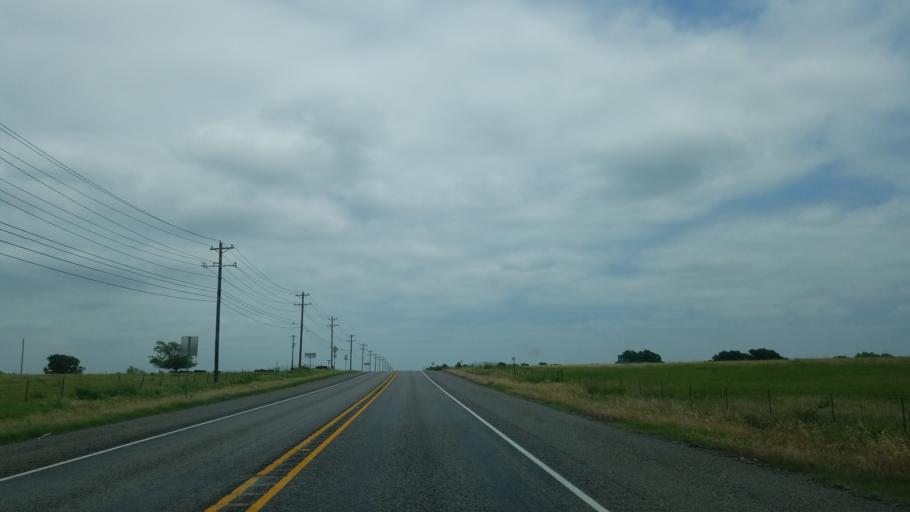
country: US
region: Texas
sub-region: Denton County
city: Aubrey
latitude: 33.3072
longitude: -97.0582
